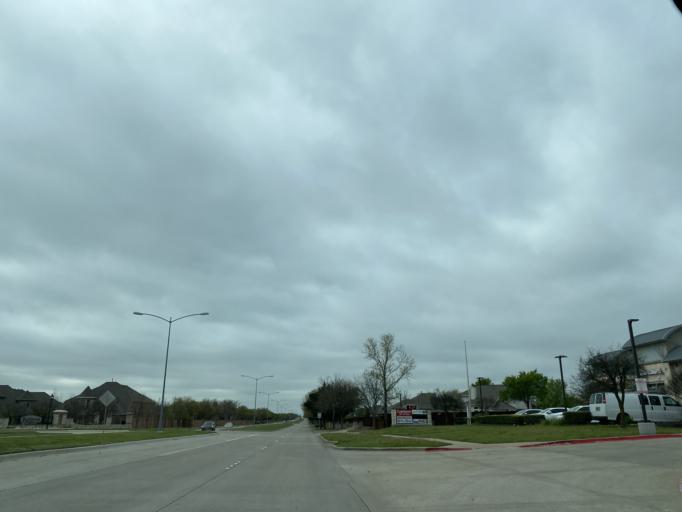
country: US
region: Texas
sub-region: Collin County
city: Fairview
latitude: 33.1287
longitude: -96.6287
